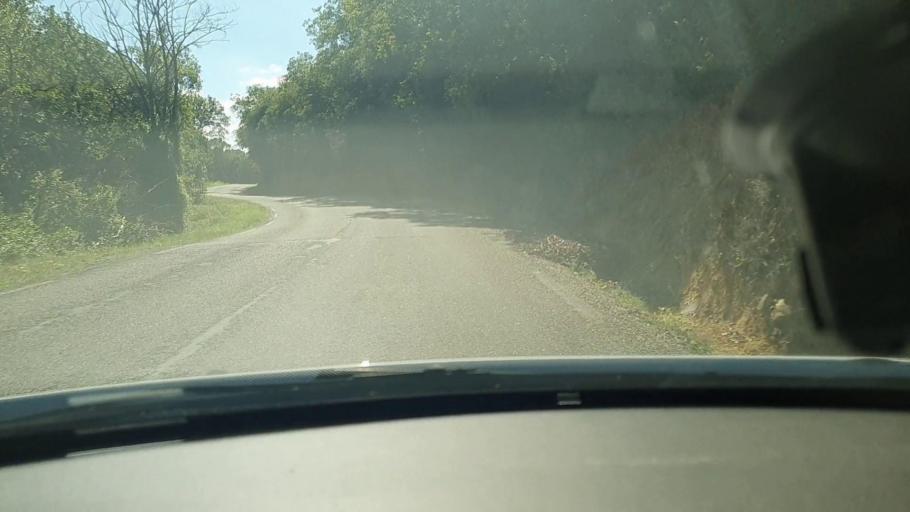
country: FR
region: Languedoc-Roussillon
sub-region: Departement du Gard
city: Sabran
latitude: 44.1830
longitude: 4.5240
